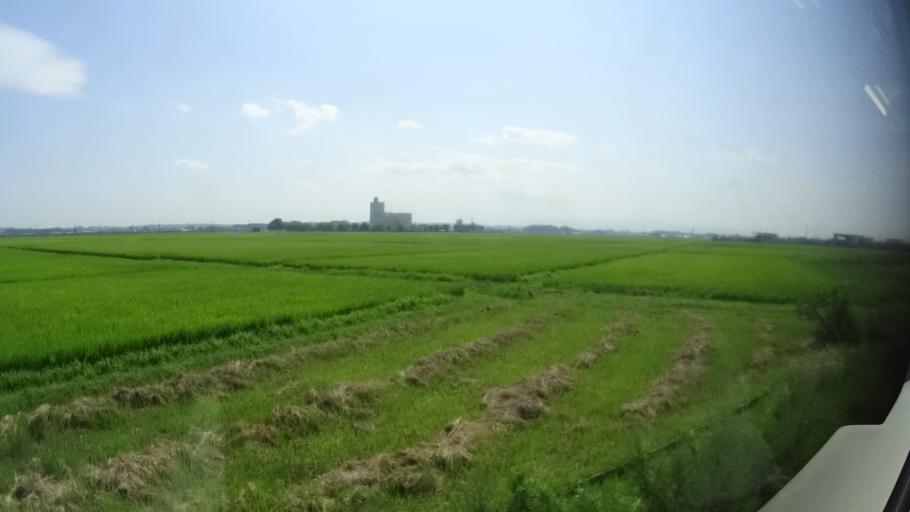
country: JP
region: Miyagi
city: Wakuya
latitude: 38.5479
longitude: 141.1035
